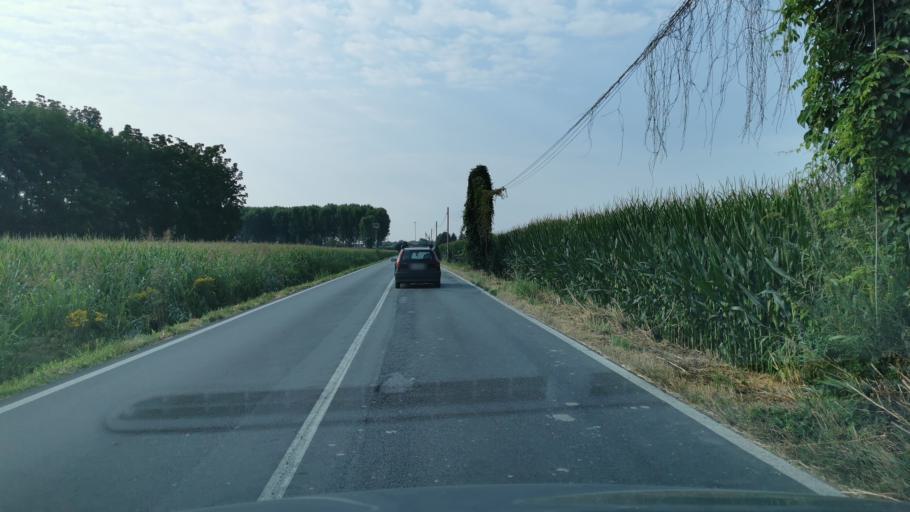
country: IT
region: Piedmont
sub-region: Provincia di Torino
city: Cercenasco
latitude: 44.8712
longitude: 7.4954
